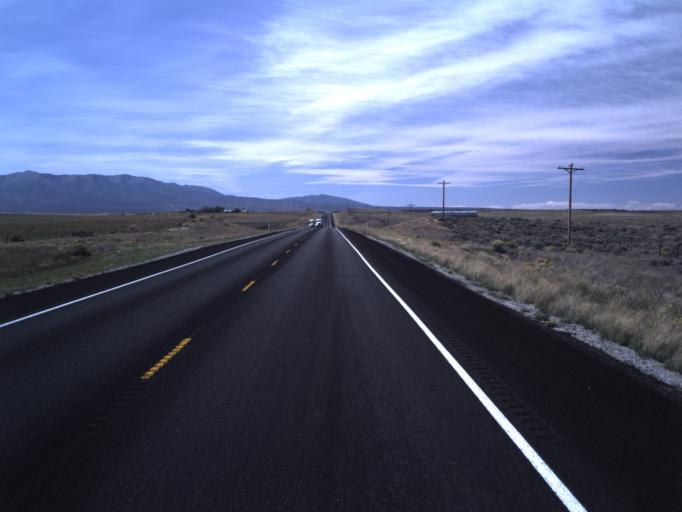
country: US
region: Utah
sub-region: San Juan County
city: Monticello
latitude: 37.8486
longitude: -109.1579
